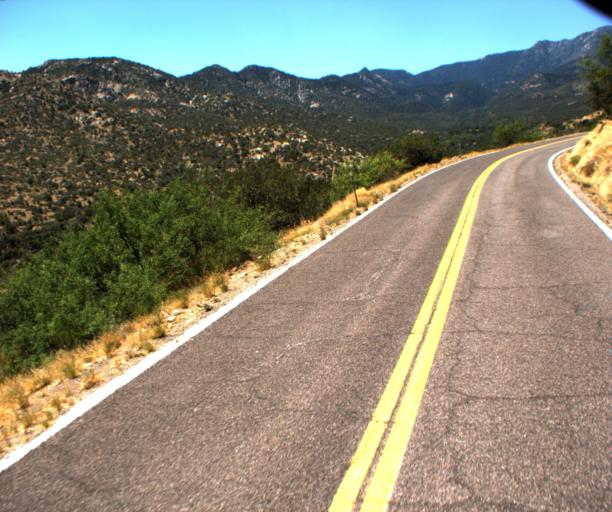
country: US
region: Arizona
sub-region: Graham County
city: Swift Trail Junction
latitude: 32.6745
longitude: -109.7809
